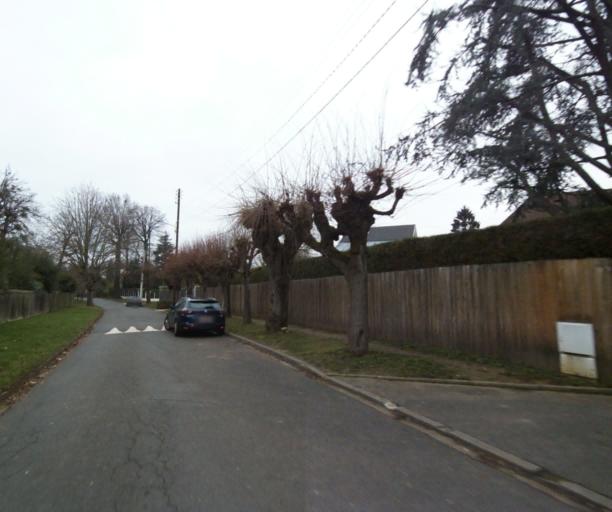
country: FR
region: Ile-de-France
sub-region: Departement des Hauts-de-Seine
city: Vaucresson
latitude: 48.8432
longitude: 2.1558
